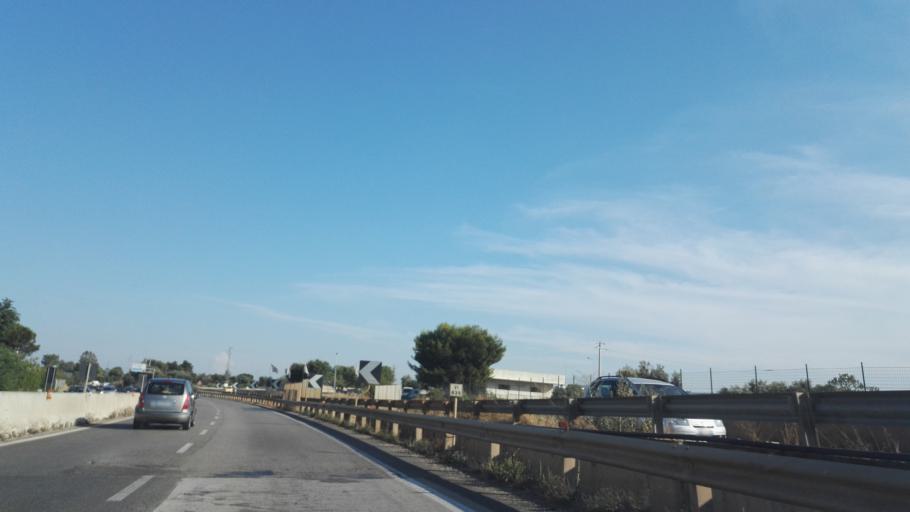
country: IT
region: Apulia
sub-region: Provincia di Bari
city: Polignano a Mare
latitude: 40.9907
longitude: 17.2080
